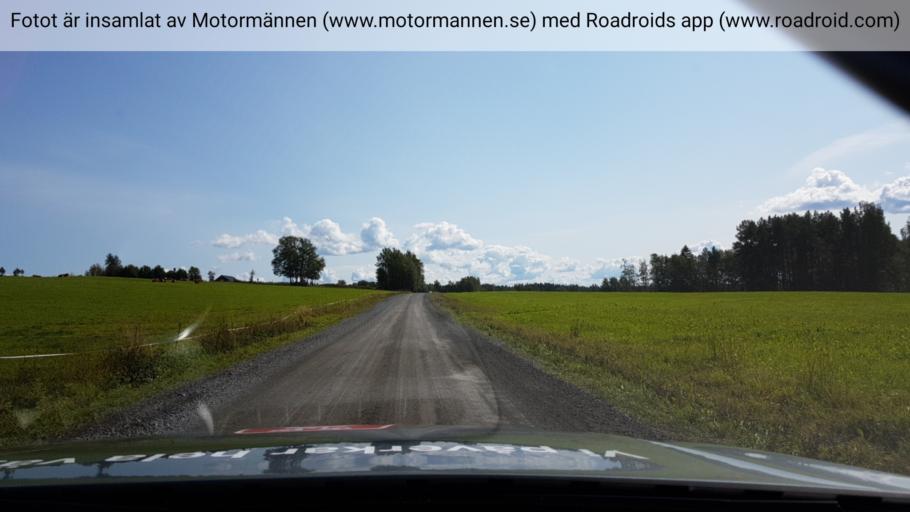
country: SE
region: Jaemtland
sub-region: OEstersunds Kommun
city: Ostersund
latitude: 63.0792
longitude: 14.5038
